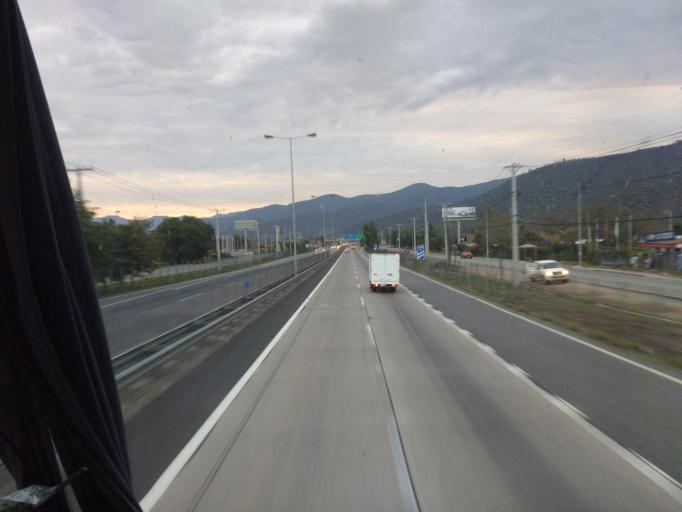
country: CL
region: Santiago Metropolitan
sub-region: Provincia de Chacabuco
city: Lampa
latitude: -33.4243
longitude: -71.0413
